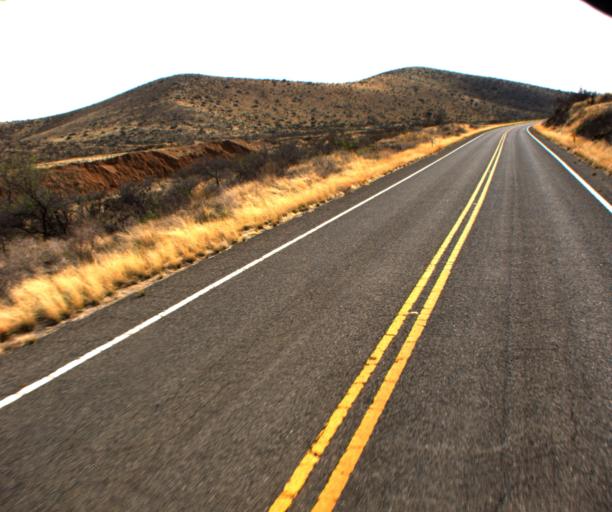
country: US
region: Arizona
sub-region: Cochise County
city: Willcox
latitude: 32.1834
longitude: -109.6526
